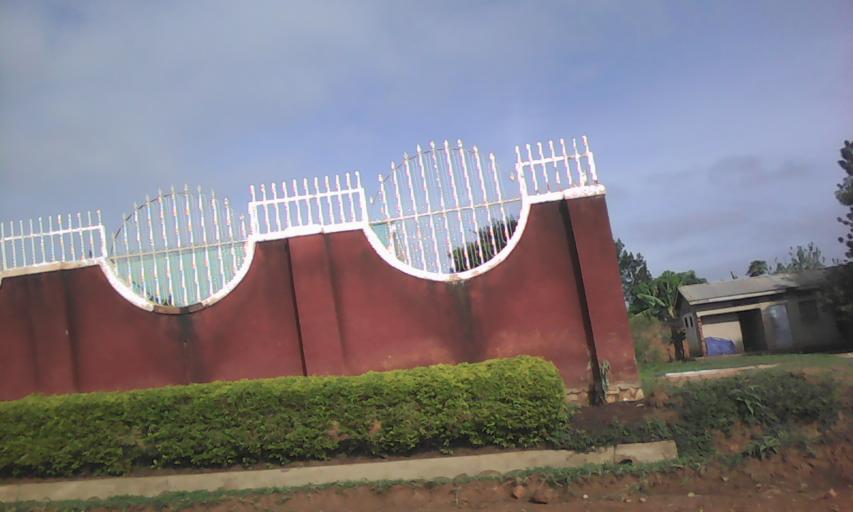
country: UG
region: Eastern Region
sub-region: Mbale District
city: Mbale
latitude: 1.0755
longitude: 34.1886
